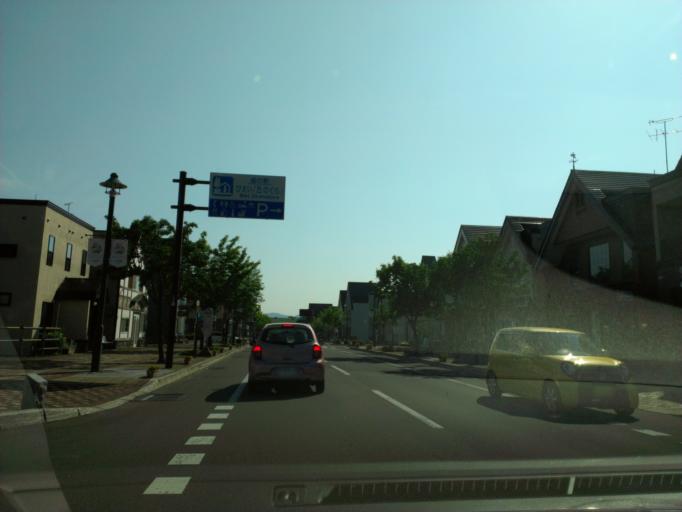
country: JP
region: Hokkaido
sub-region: Asahikawa-shi
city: Asahikawa
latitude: 43.5926
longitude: 142.4653
